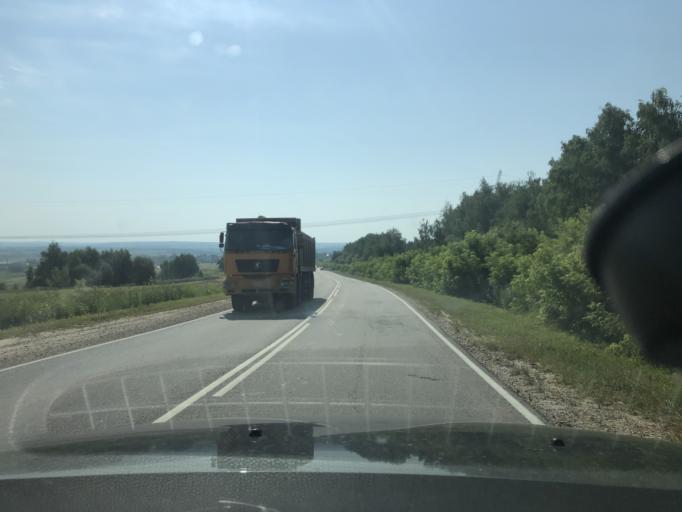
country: RU
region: Tula
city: Dubna
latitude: 54.1164
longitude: 37.0828
